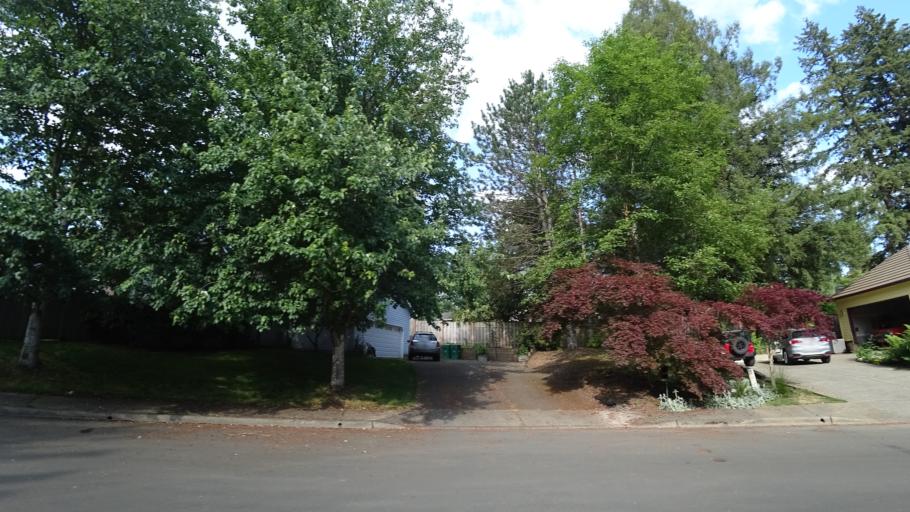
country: US
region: Oregon
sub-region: Washington County
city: Garden Home-Whitford
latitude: 45.4622
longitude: -122.7491
